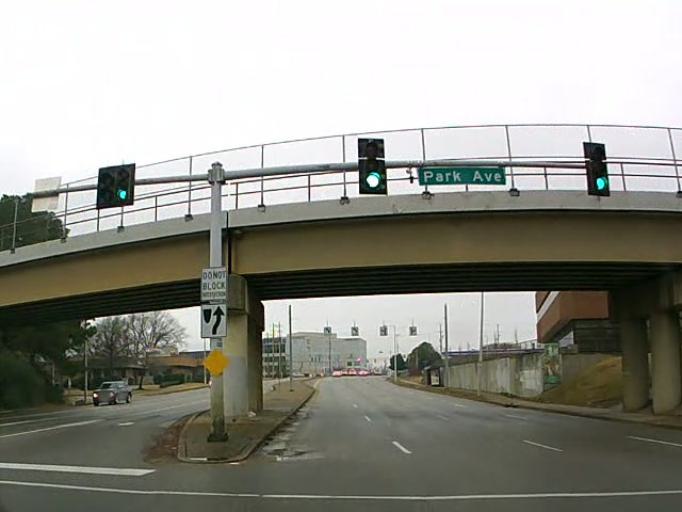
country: US
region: Tennessee
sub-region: Shelby County
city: Germantown
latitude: 35.1008
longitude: -89.8592
